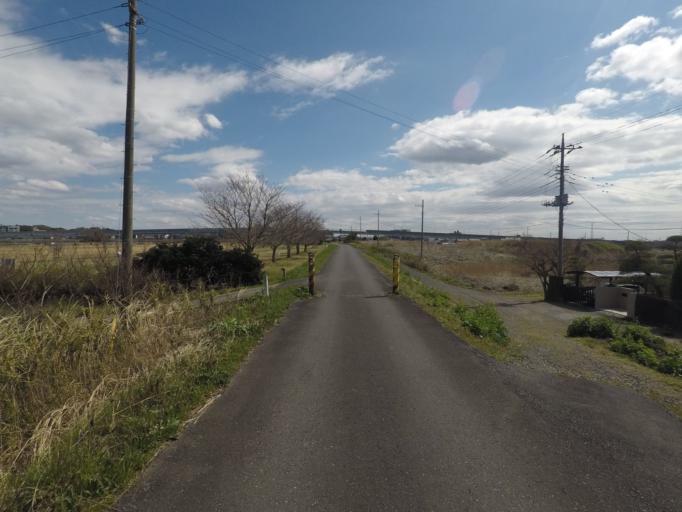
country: JP
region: Ibaraki
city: Fujishiro
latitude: 35.9375
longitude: 140.1295
